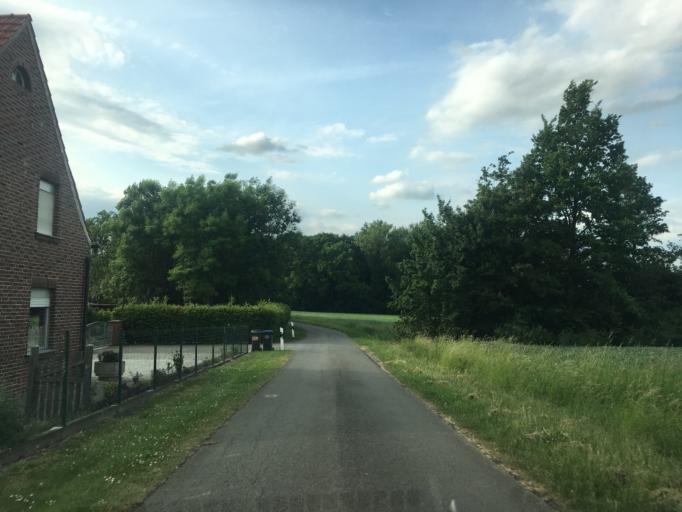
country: DE
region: North Rhine-Westphalia
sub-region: Regierungsbezirk Munster
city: Altenberge
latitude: 52.0230
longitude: 7.5417
